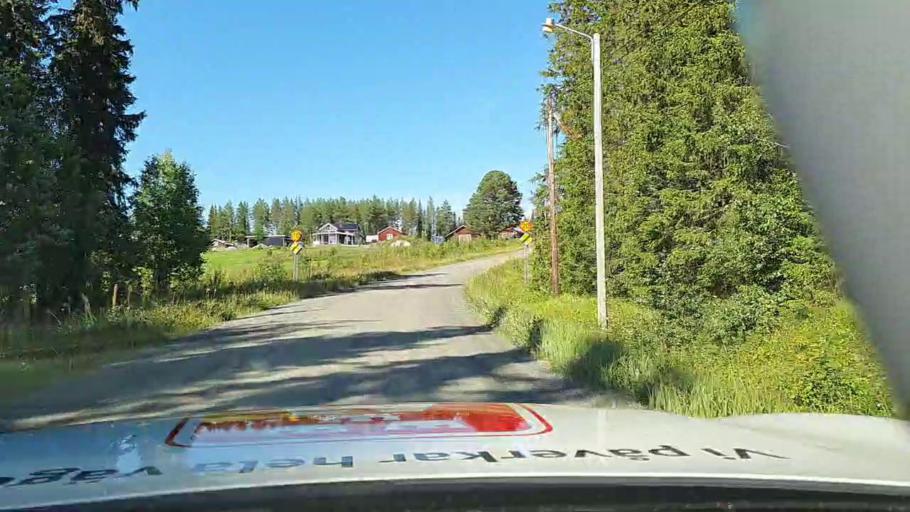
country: SE
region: Jaemtland
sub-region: Krokoms Kommun
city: Krokom
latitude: 63.6822
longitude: 14.6033
